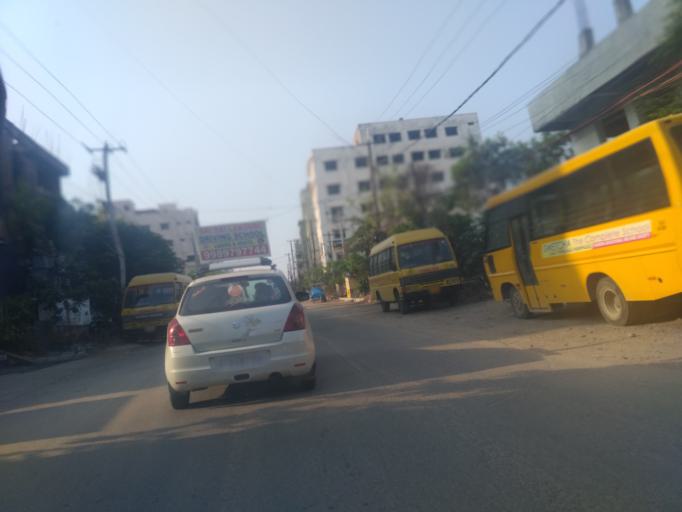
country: IN
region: Telangana
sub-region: Rangareddi
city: Kukatpalli
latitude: 17.4499
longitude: 78.3918
